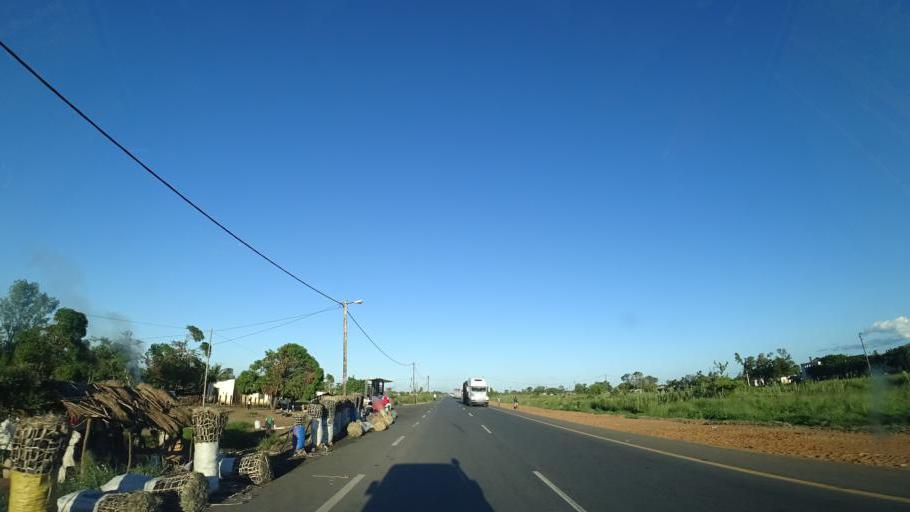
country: MZ
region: Sofala
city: Dondo
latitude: -19.3316
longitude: 34.3168
